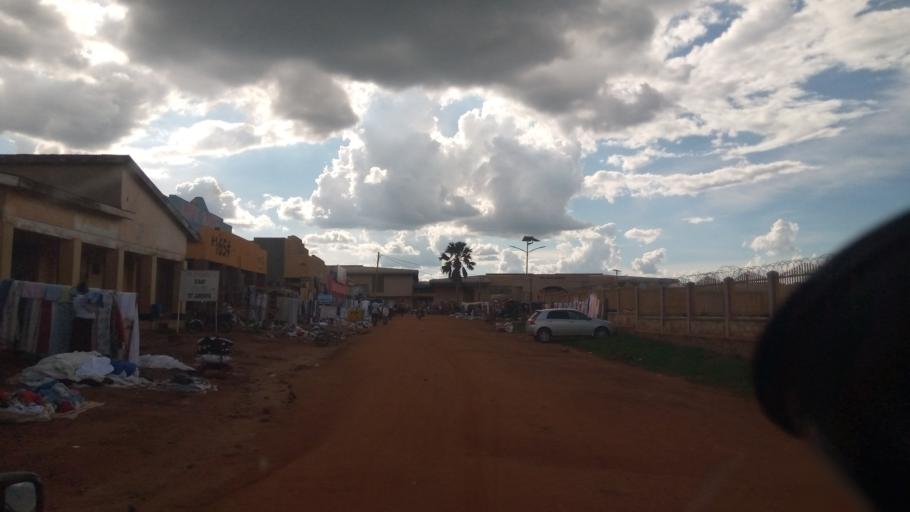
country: UG
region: Northern Region
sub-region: Lira District
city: Lira
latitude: 2.2429
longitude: 32.8988
